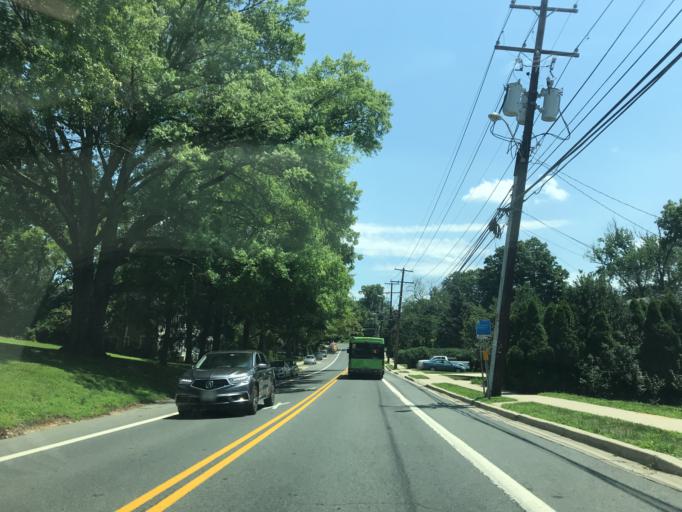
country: US
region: Maryland
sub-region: Montgomery County
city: Kensington
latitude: 39.0288
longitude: -77.0818
